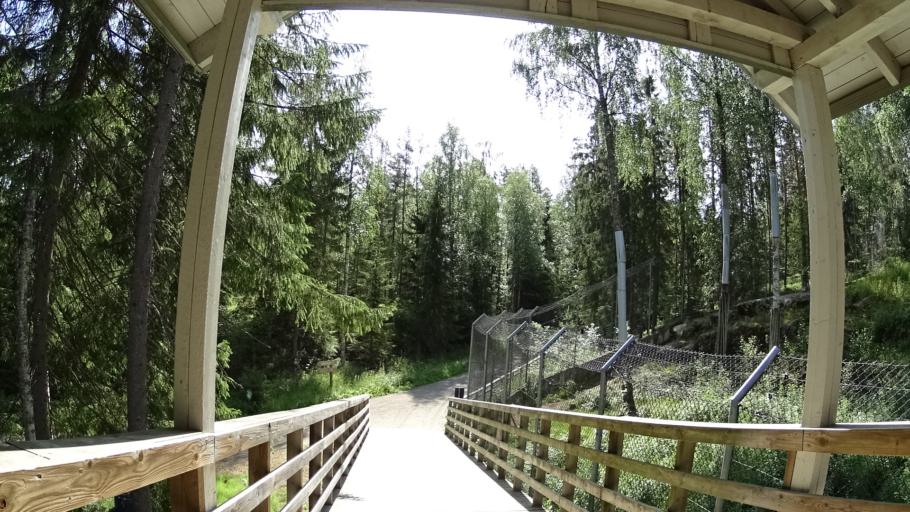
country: FI
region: Southern Ostrobothnia
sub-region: Kuusiokunnat
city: AEhtaeri
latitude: 62.5379
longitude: 24.1874
